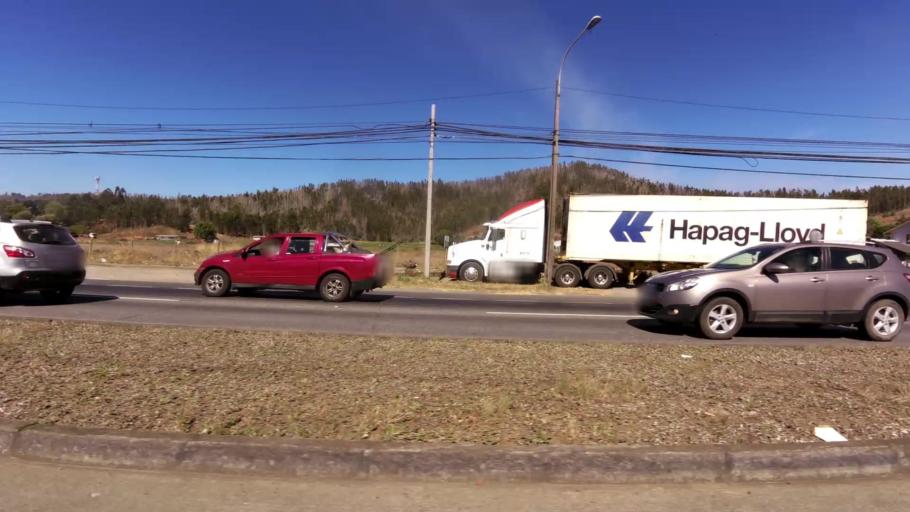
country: CL
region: Biobio
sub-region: Provincia de Concepcion
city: Concepcion
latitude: -36.7906
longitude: -73.0247
